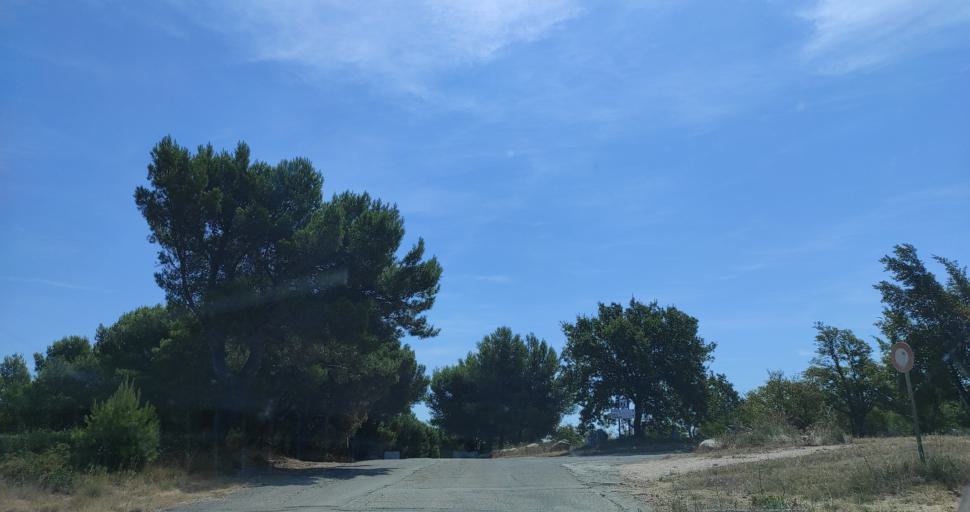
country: FR
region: Provence-Alpes-Cote d'Azur
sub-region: Departement des Bouches-du-Rhone
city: Martigues
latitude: 43.4177
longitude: 5.0420
